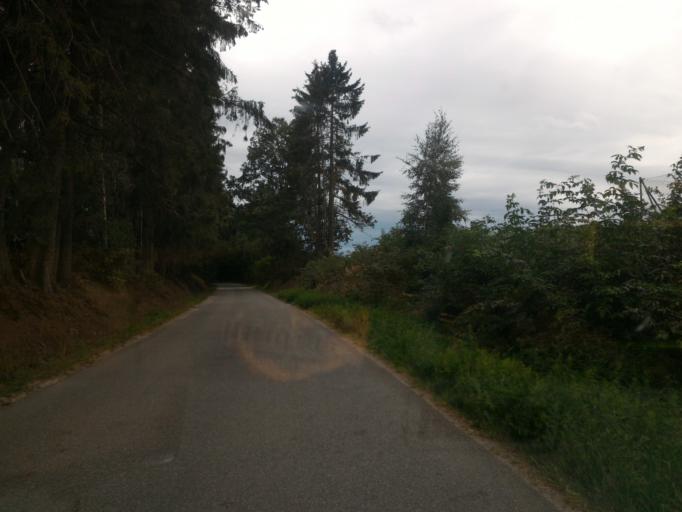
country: CZ
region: Vysocina
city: Knezice
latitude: 49.2371
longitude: 15.5991
